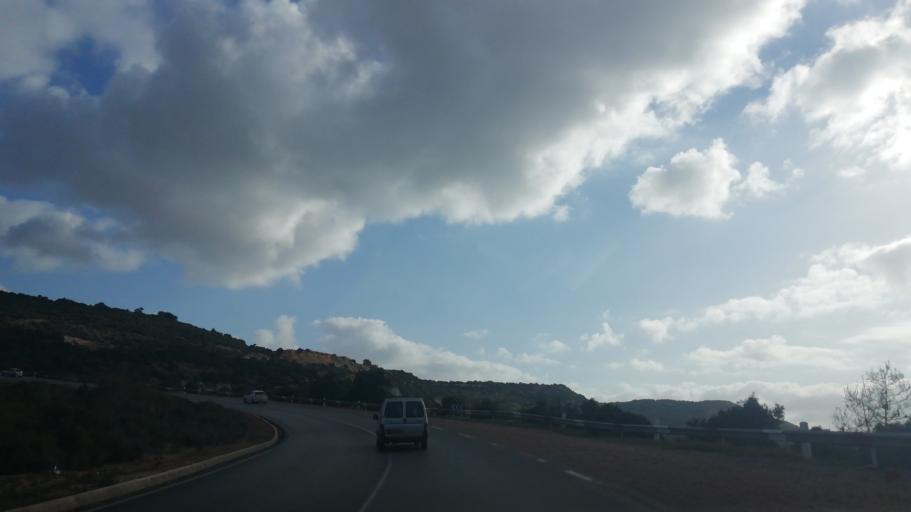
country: DZ
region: Relizane
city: Mazouna
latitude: 36.2375
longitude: 0.5415
